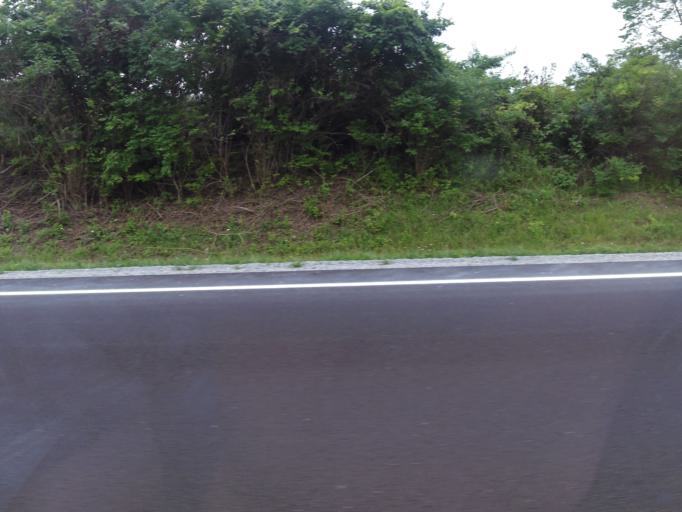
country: US
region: Ohio
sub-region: Clinton County
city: Blanchester
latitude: 39.2063
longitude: -83.9208
